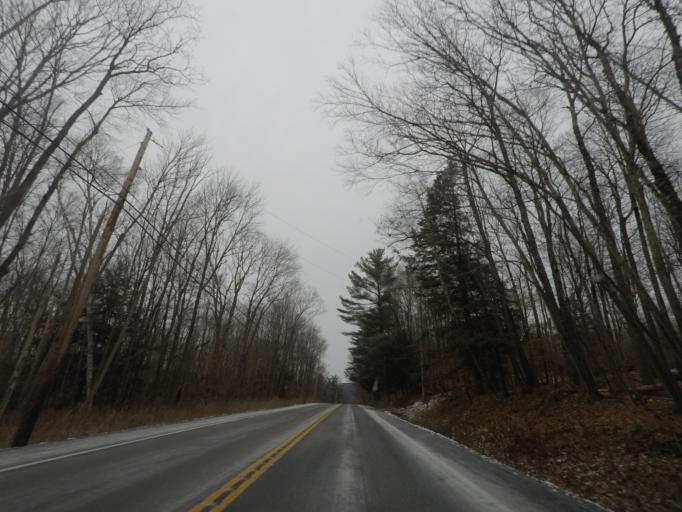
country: US
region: New York
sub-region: Rensselaer County
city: Hoosick Falls
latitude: 42.7599
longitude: -73.3730
